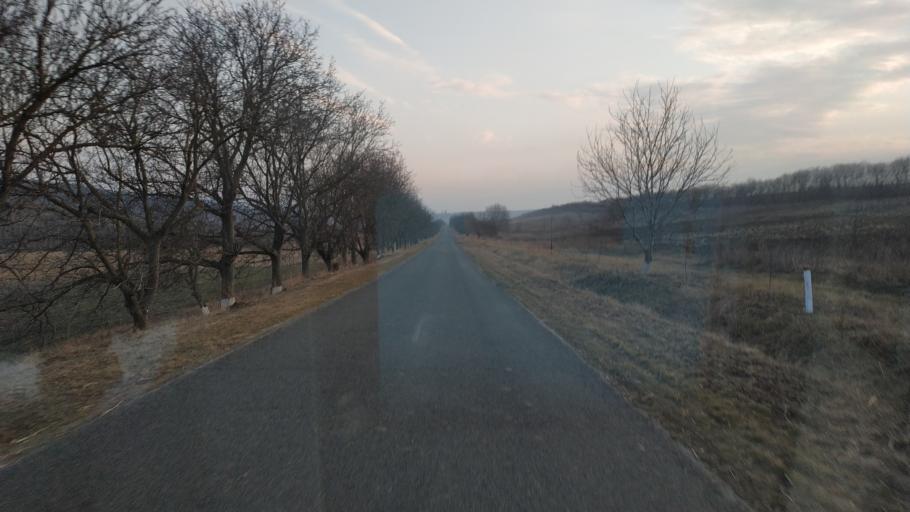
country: MD
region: Hincesti
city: Dancu
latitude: 46.6922
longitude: 28.3361
